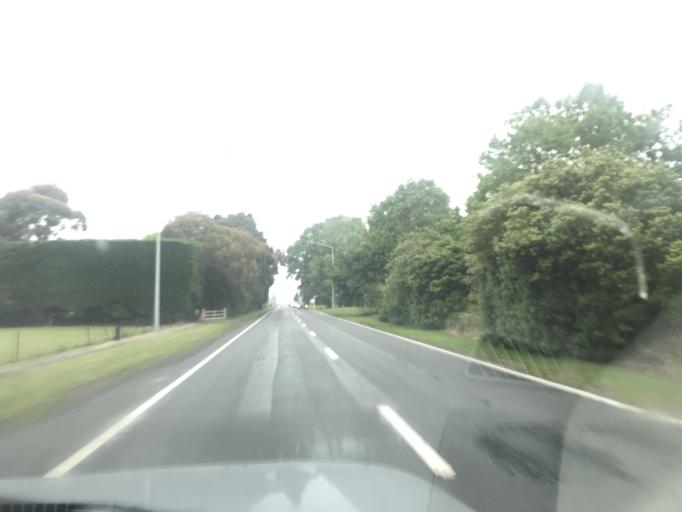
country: NZ
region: Canterbury
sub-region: Selwyn District
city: Darfield
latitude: -43.5012
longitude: 172.2173
